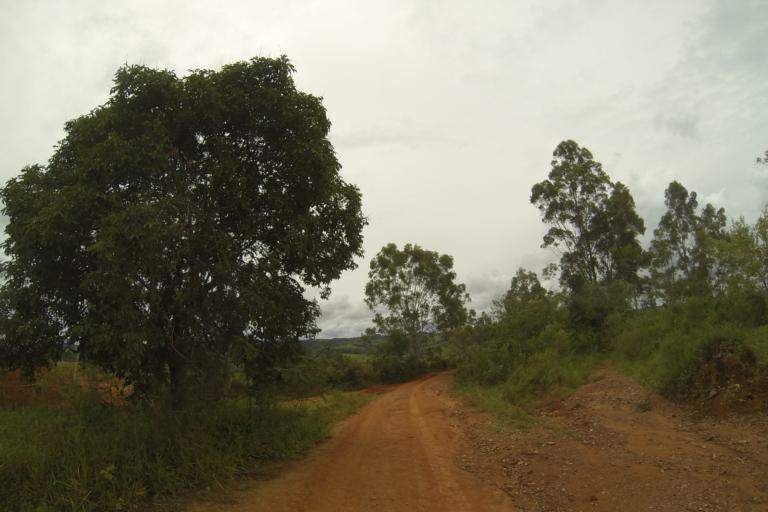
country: BR
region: Minas Gerais
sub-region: Ibia
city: Ibia
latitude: -19.6833
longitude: -46.6810
